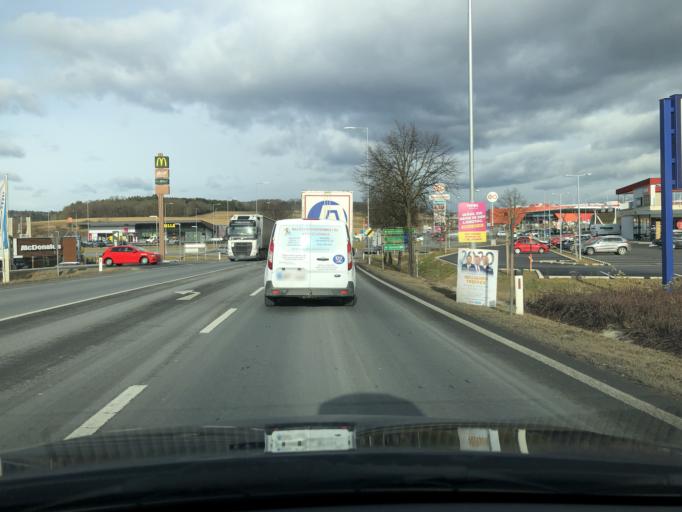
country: AT
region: Burgenland
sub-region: Politischer Bezirk Oberwart
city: Oberwart
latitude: 47.2830
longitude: 16.1877
